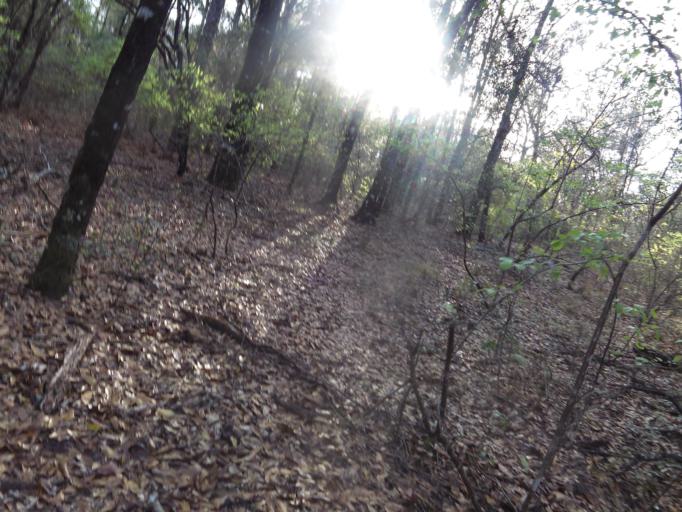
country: US
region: Florida
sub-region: Clay County
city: Middleburg
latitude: 30.1445
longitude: -81.9530
